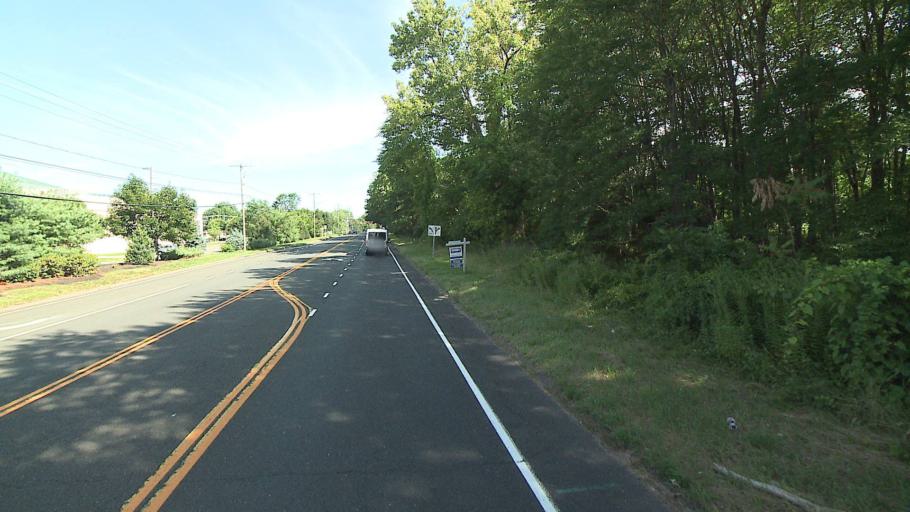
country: US
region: Connecticut
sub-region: Hartford County
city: Blue Hills
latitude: 41.8331
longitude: -72.6979
